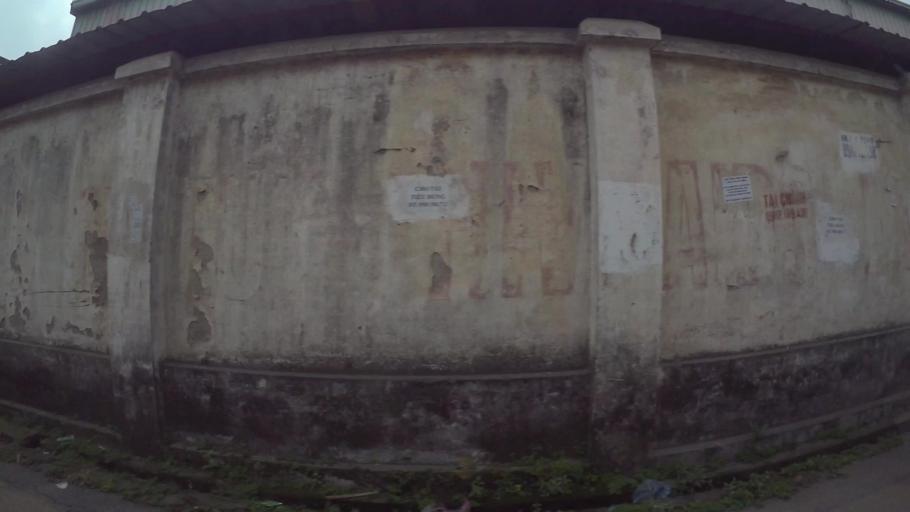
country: VN
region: Ha Noi
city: Trau Quy
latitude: 21.0745
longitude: 105.9079
